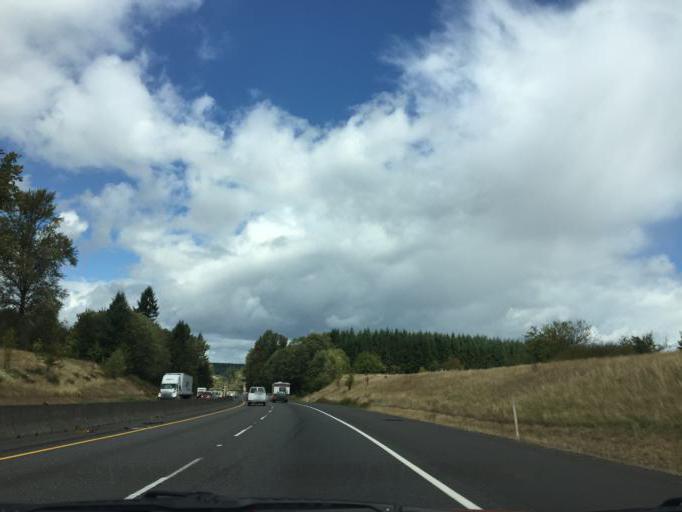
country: US
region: Washington
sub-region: Lewis County
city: Winlock
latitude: 46.4095
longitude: -122.8894
